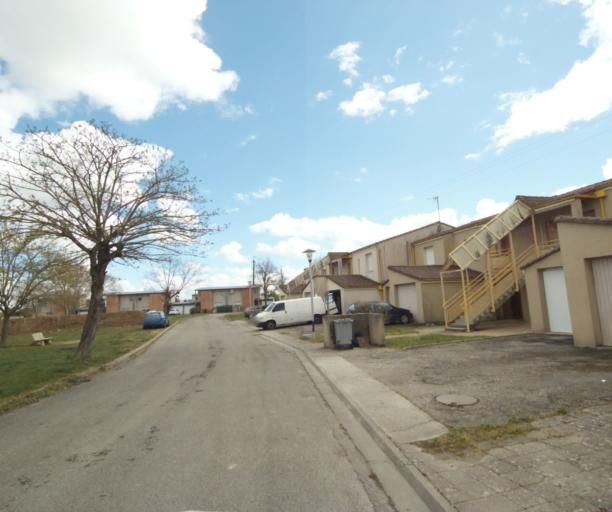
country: FR
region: Midi-Pyrenees
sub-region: Departement de l'Ariege
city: Saverdun
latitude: 43.2351
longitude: 1.5839
